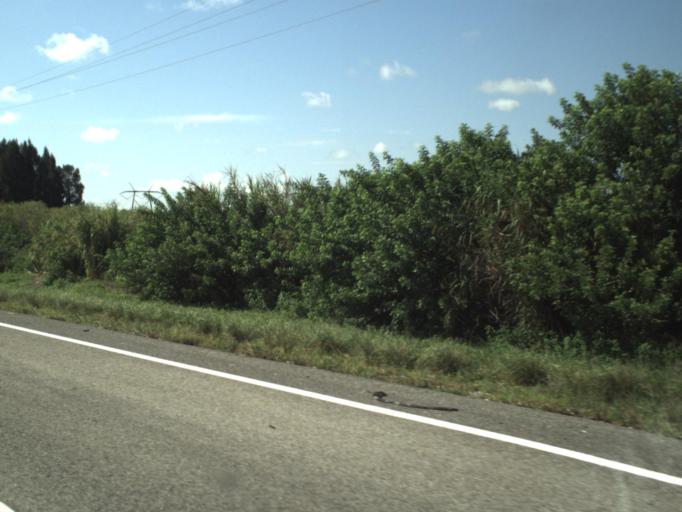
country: US
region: Florida
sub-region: Broward County
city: Weston
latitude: 26.3347
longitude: -80.5379
